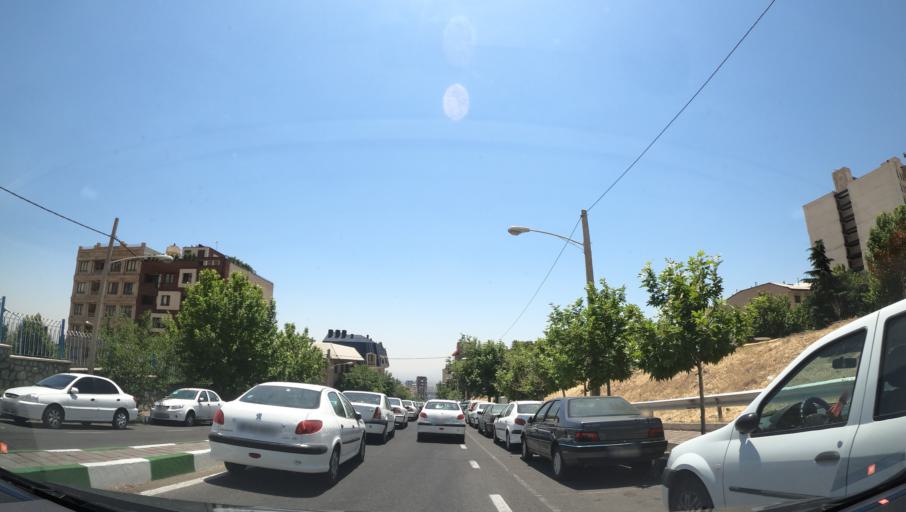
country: IR
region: Tehran
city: Tajrish
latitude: 35.8122
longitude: 51.3989
